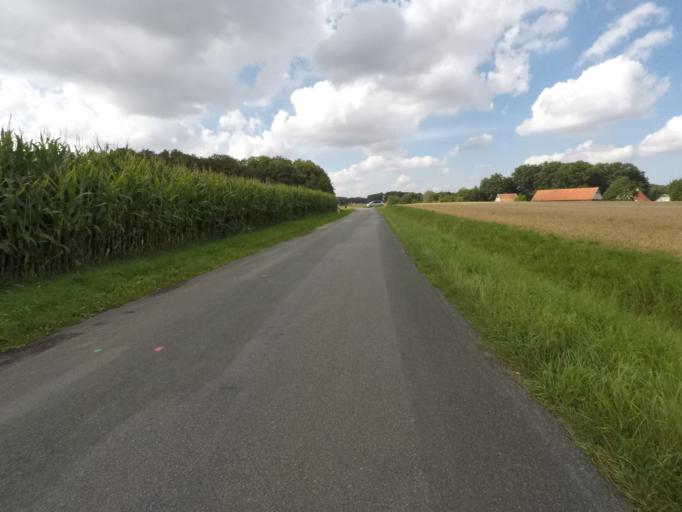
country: DE
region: North Rhine-Westphalia
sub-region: Regierungsbezirk Detmold
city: Werther
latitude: 52.0729
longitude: 8.4532
